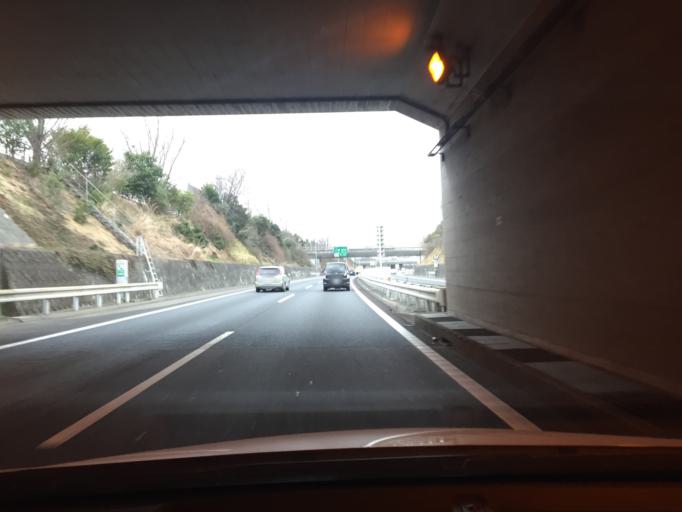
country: JP
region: Saitama
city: Sayama
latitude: 35.8220
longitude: 139.3723
